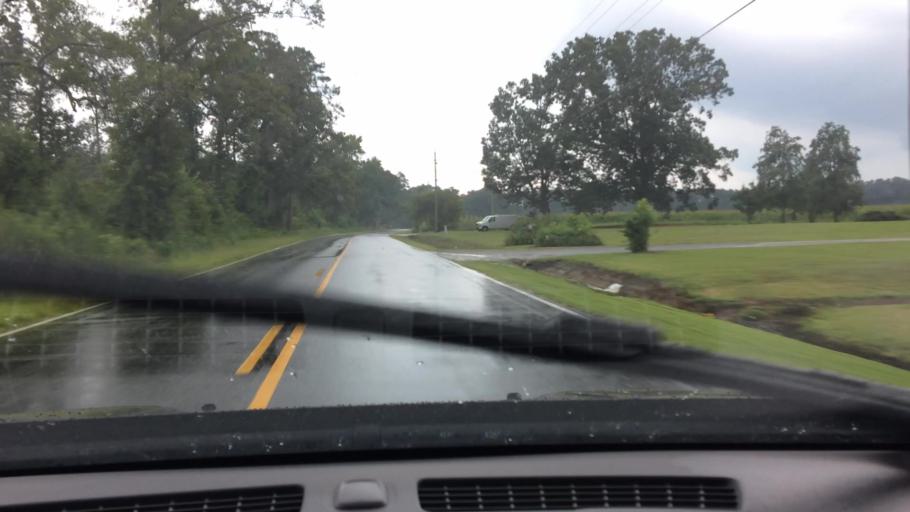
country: US
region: North Carolina
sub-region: Pitt County
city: Winterville
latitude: 35.5101
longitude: -77.3815
